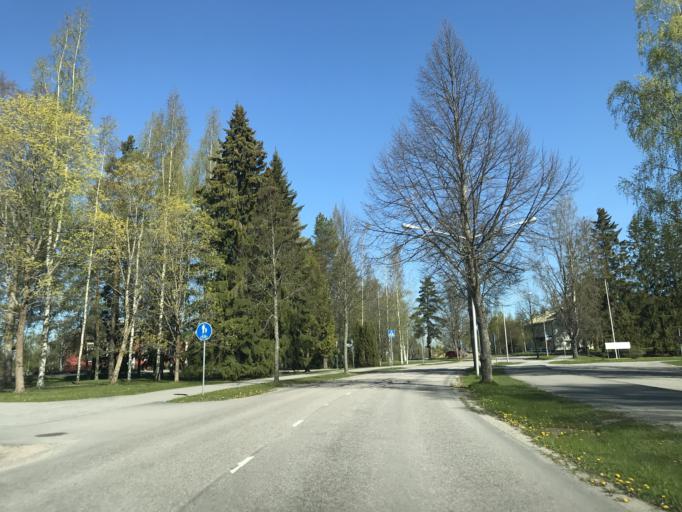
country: FI
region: Paijanne Tavastia
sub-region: Lahti
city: Orimattila
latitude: 60.8090
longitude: 25.7371
